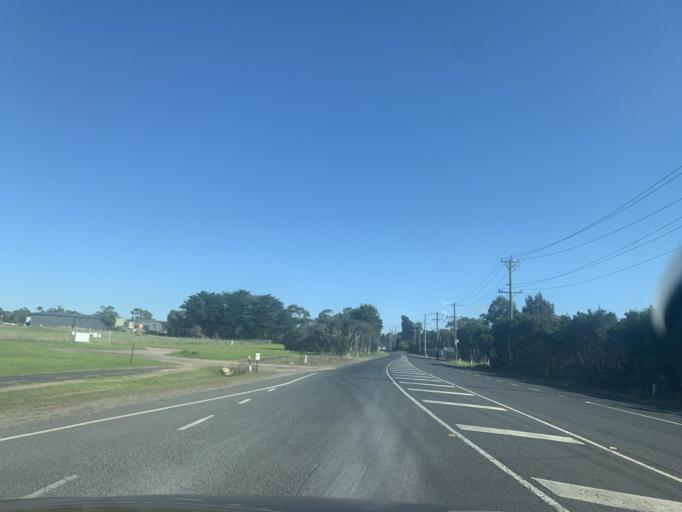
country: AU
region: Victoria
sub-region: Mornington Peninsula
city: Hastings
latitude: -38.2889
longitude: 145.1946
